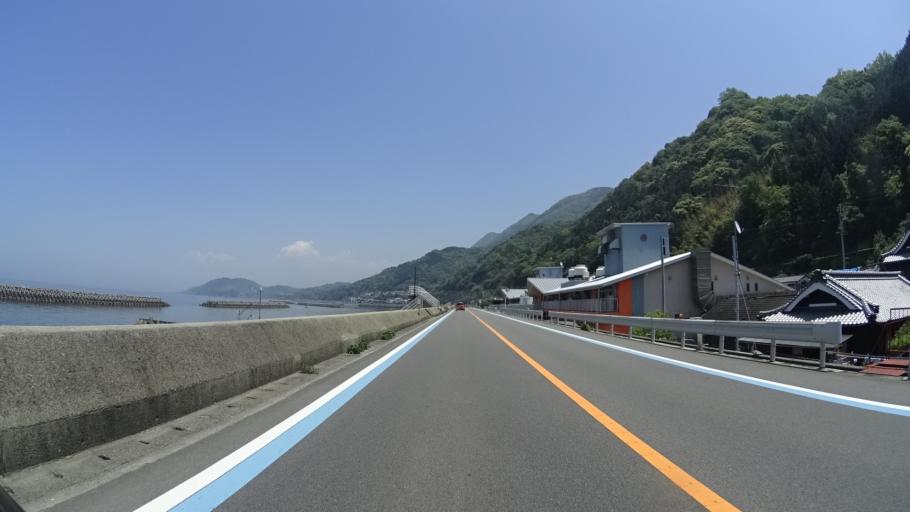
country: JP
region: Ehime
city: Iyo
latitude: 33.6907
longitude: 132.6419
